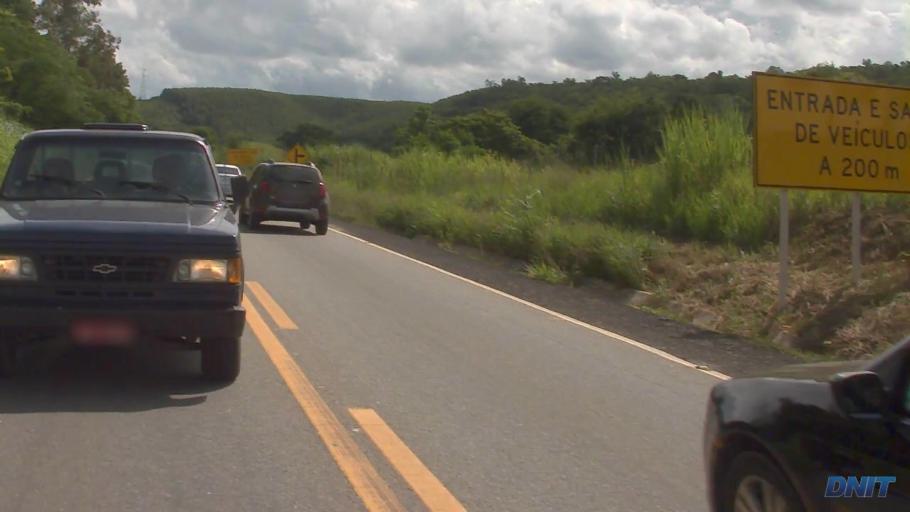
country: BR
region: Minas Gerais
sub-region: Ipaba
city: Ipaba
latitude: -19.3949
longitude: -42.4839
